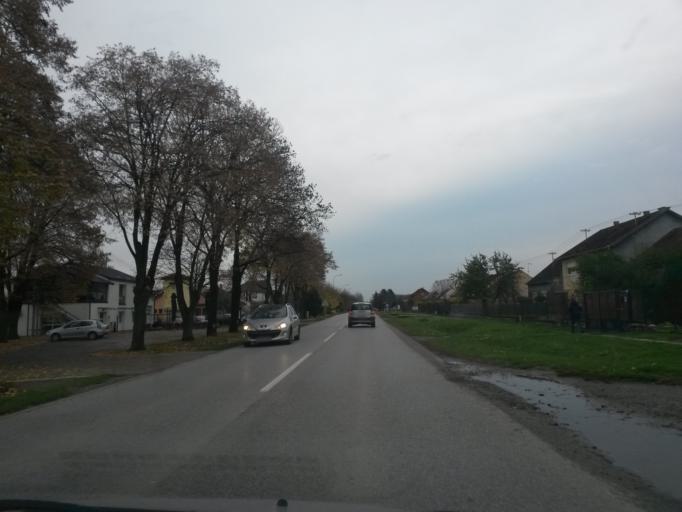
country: HR
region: Osjecko-Baranjska
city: Darda
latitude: 45.6230
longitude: 18.7027
